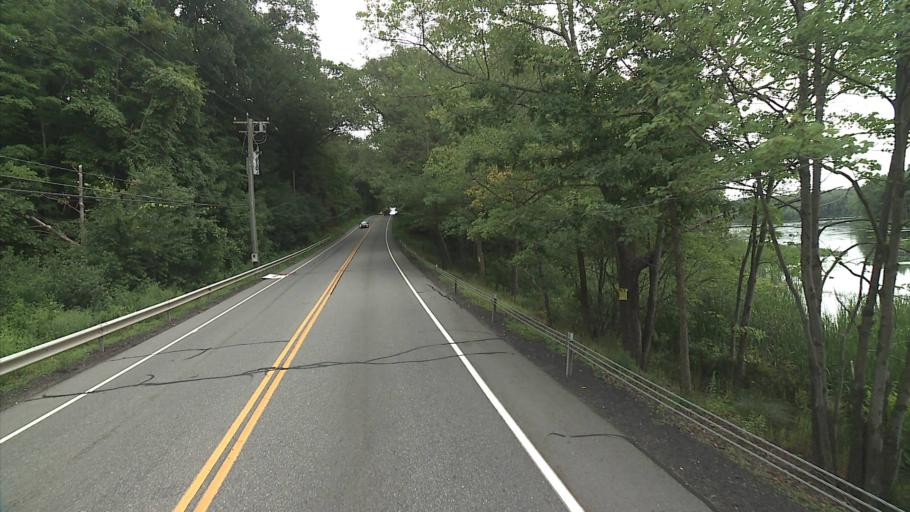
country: US
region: Connecticut
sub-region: Tolland County
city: Storrs
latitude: 41.8716
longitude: -72.2137
